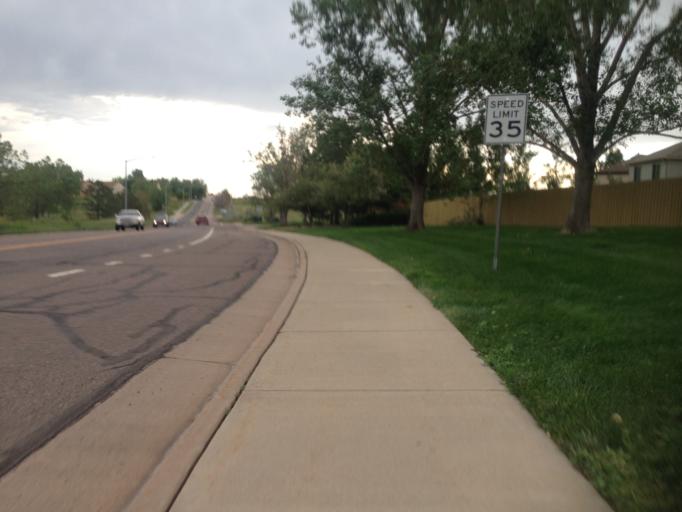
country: US
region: Colorado
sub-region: Boulder County
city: Superior
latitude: 39.9384
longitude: -105.1470
